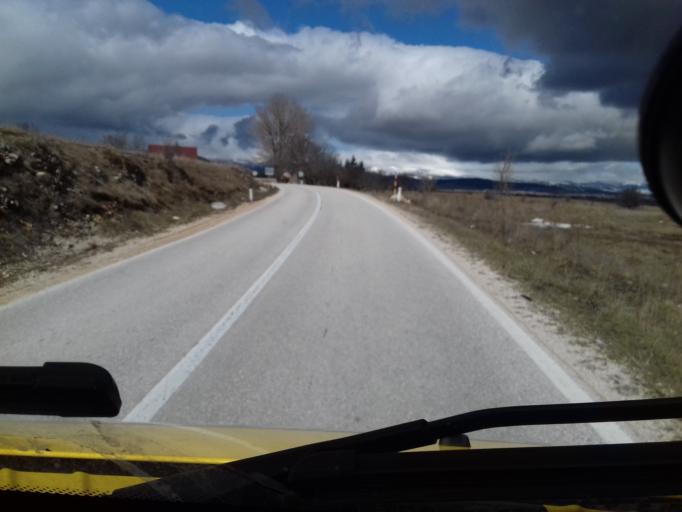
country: BA
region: Federation of Bosnia and Herzegovina
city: Dreznica
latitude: 43.6185
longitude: 17.2638
